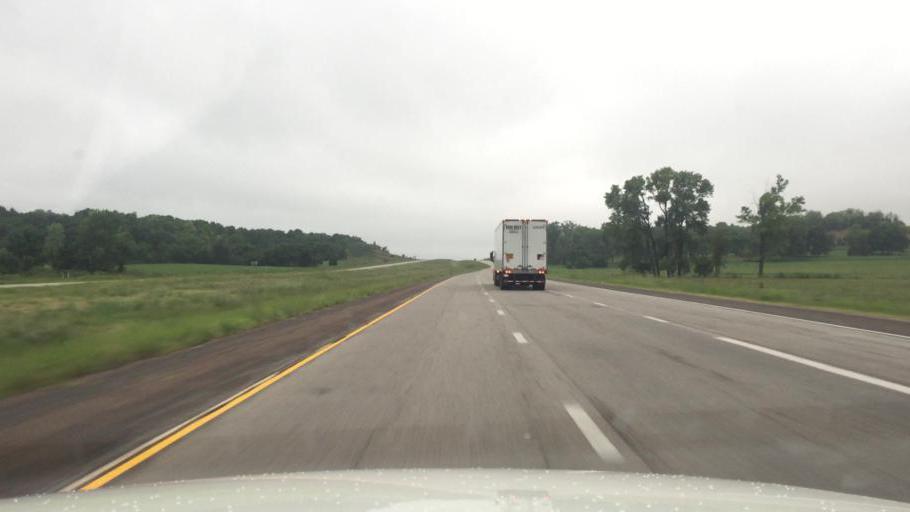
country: US
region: Kansas
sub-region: Montgomery County
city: Cherryvale
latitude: 37.2229
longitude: -95.5858
